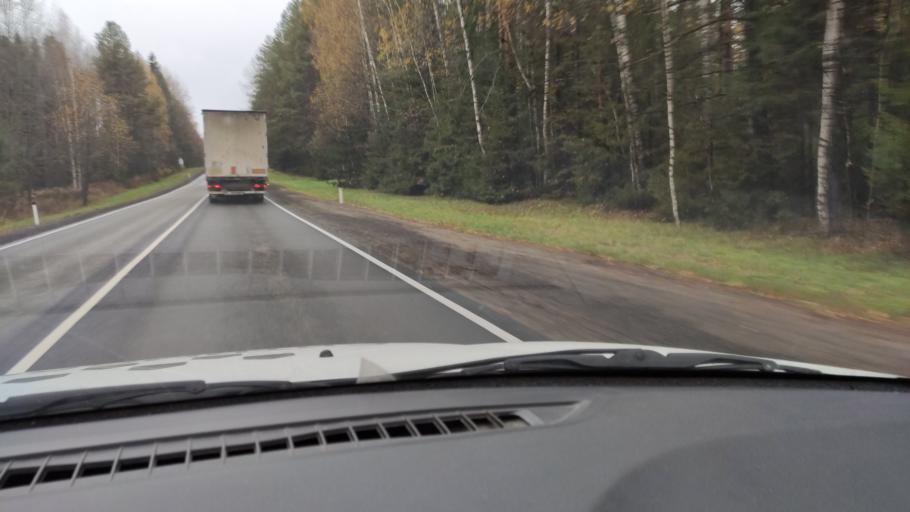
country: RU
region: Kirov
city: Belaya Kholunitsa
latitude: 58.8278
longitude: 50.6306
